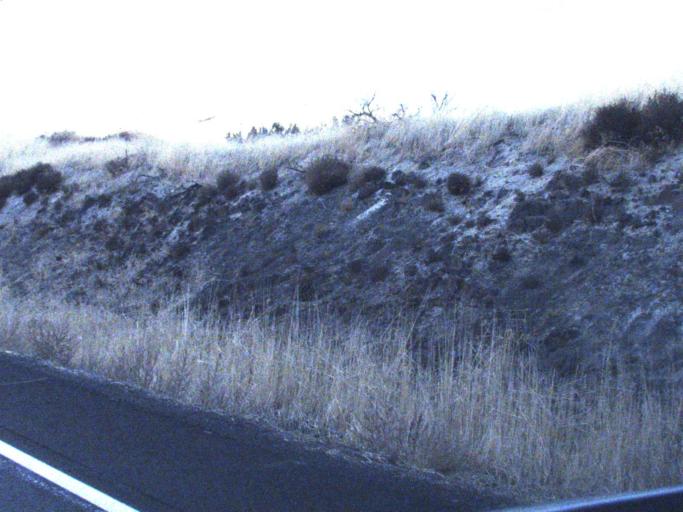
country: US
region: Washington
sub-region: Walla Walla County
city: Burbank
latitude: 46.0713
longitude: -118.7745
